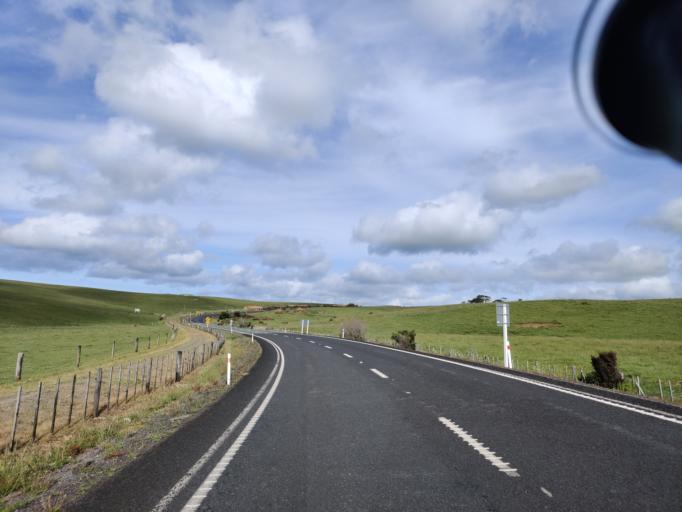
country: NZ
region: Northland
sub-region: Kaipara District
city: Dargaville
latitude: -35.7488
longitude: 173.6244
